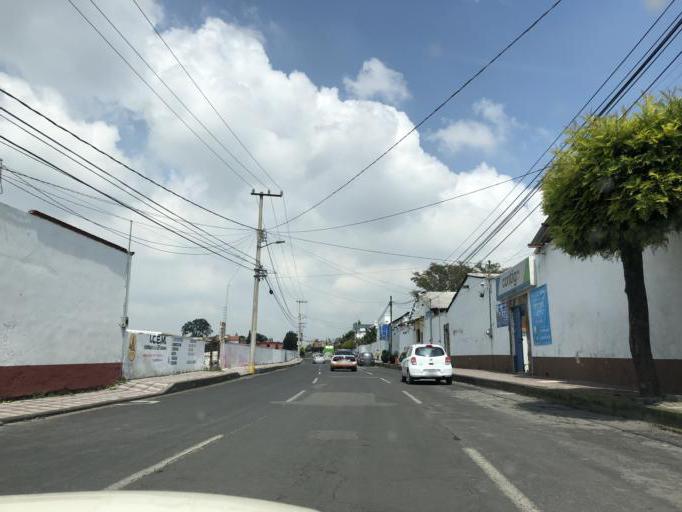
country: MX
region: Mexico
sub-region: Lerma
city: Nueva Ameyalco
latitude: 19.2852
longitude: -99.5031
